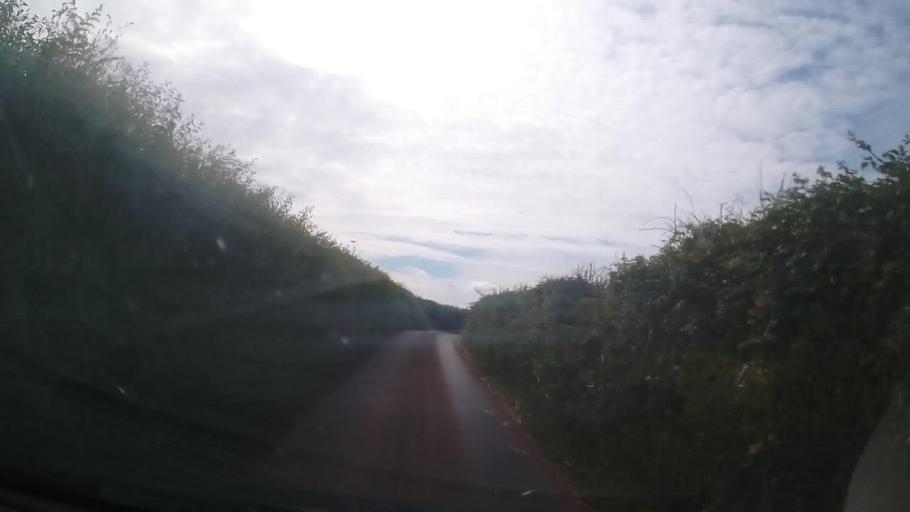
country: GB
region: England
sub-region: Devon
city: Salcombe
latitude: 50.2373
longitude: -3.6752
